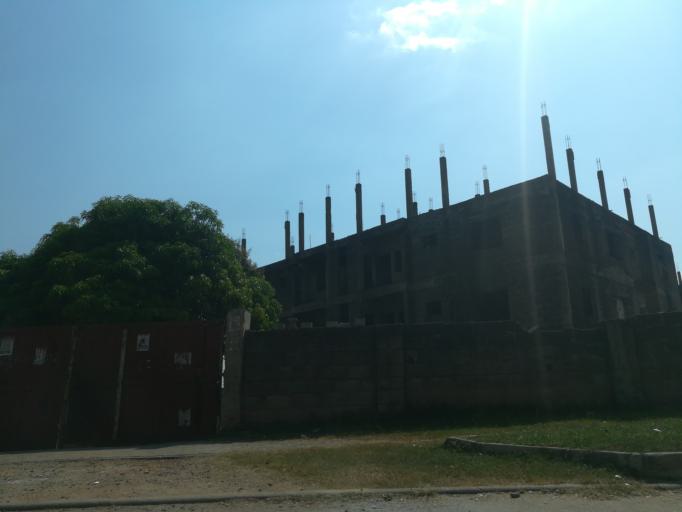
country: NG
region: Abuja Federal Capital Territory
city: Abuja
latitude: 9.0610
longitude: 7.4254
